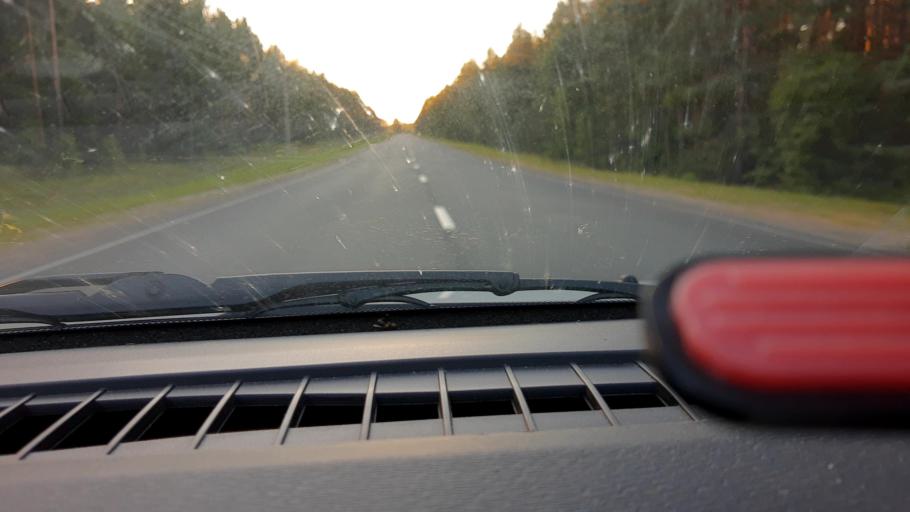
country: RU
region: Nizjnij Novgorod
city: Uren'
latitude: 57.3594
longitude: 45.6993
